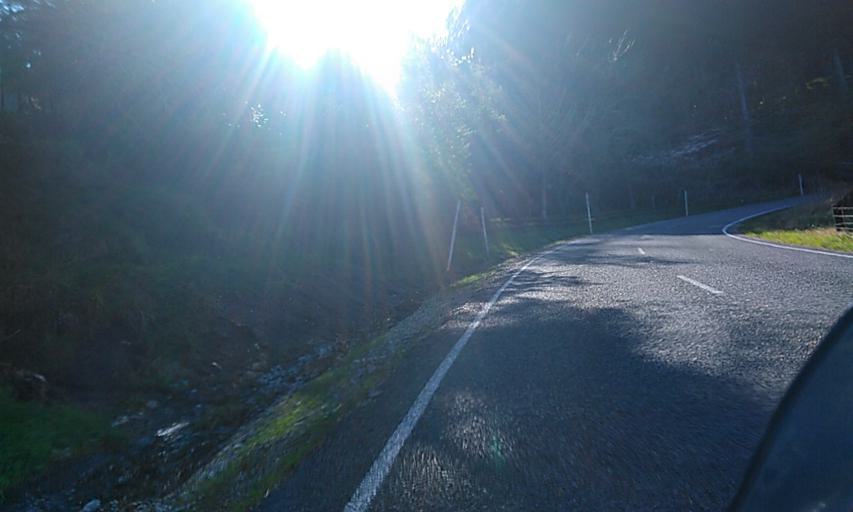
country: NZ
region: Gisborne
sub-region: Gisborne District
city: Gisborne
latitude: -38.5908
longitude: 177.9739
